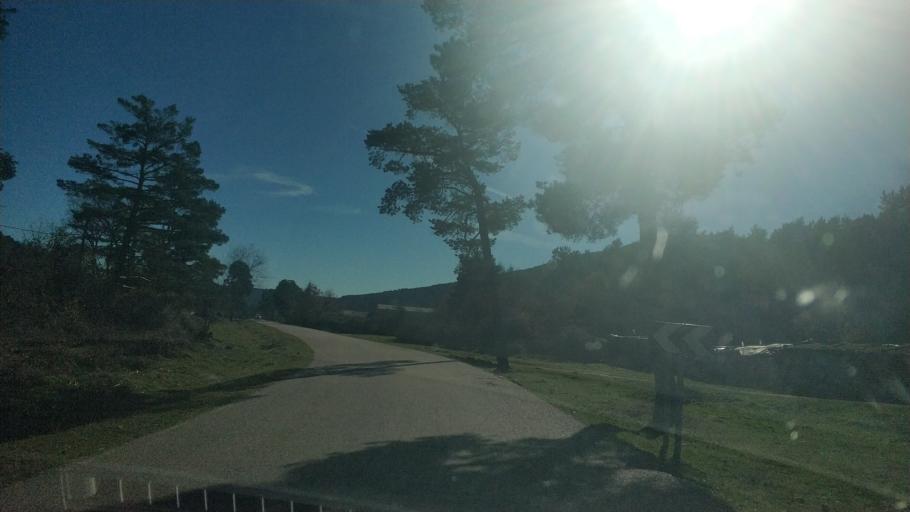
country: ES
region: Castille and Leon
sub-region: Provincia de Soria
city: Vinuesa
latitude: 41.9288
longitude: -2.7747
